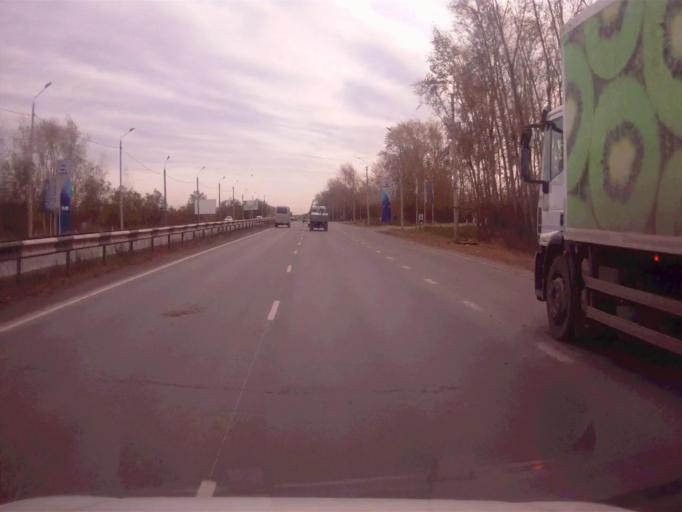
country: RU
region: Chelyabinsk
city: Novosineglazovskiy
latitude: 55.0544
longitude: 61.4086
